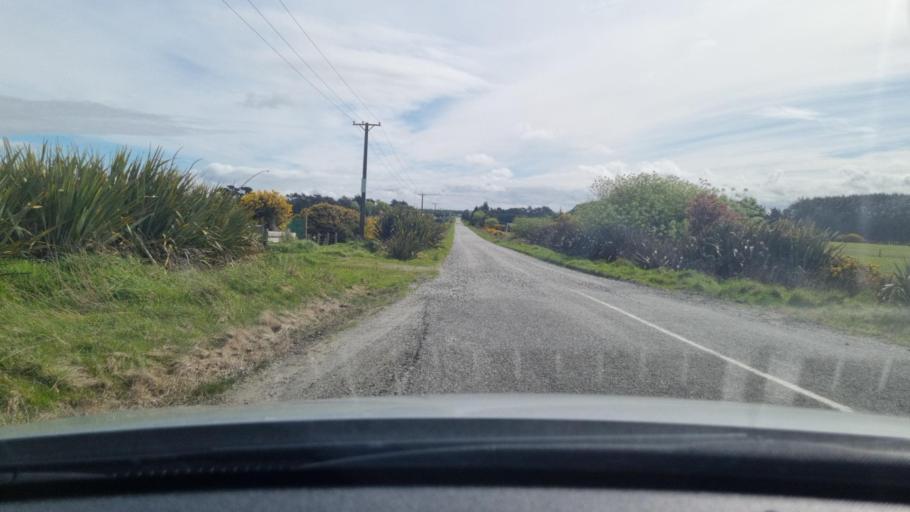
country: NZ
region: Southland
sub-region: Invercargill City
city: Invercargill
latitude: -46.4507
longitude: 168.3937
